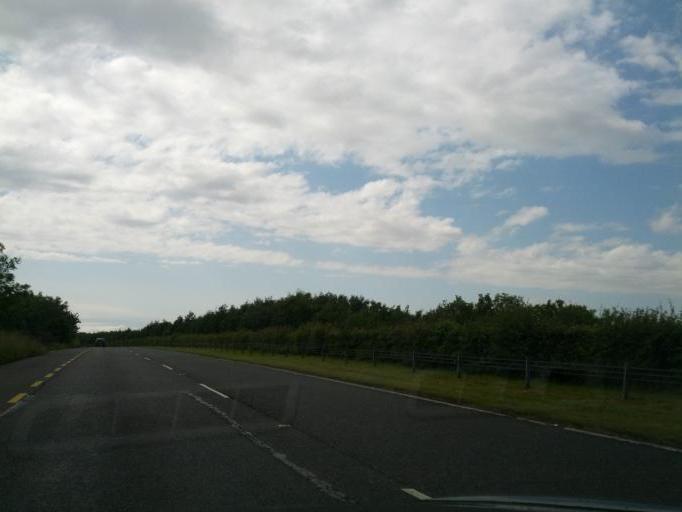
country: IE
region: Connaught
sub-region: County Galway
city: Oranmore
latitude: 53.2774
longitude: -8.9360
